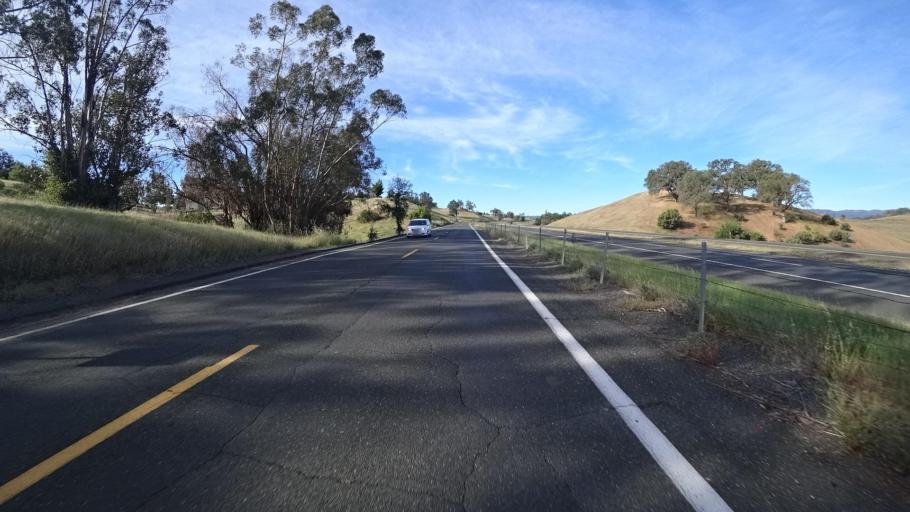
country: US
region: California
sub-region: Lake County
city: North Lakeport
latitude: 39.0963
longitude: -122.9140
